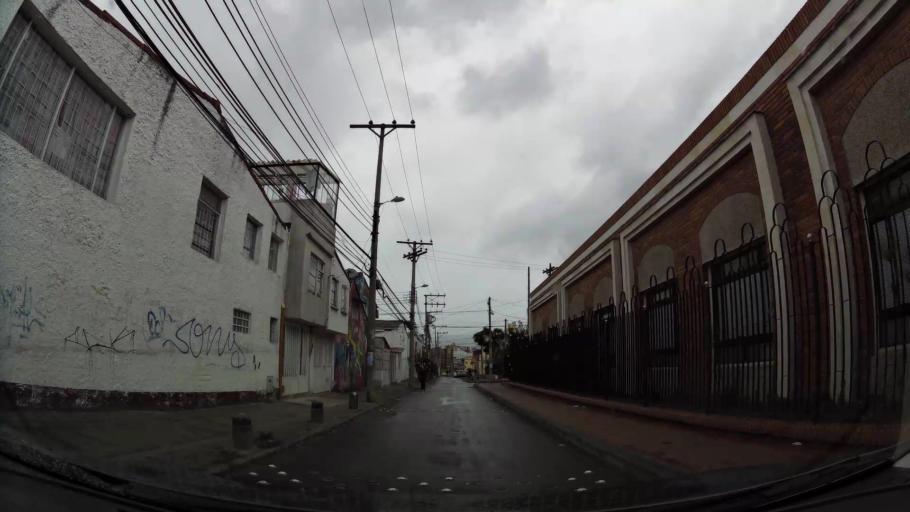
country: CO
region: Bogota D.C.
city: Barrio San Luis
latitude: 4.6997
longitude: -74.0906
